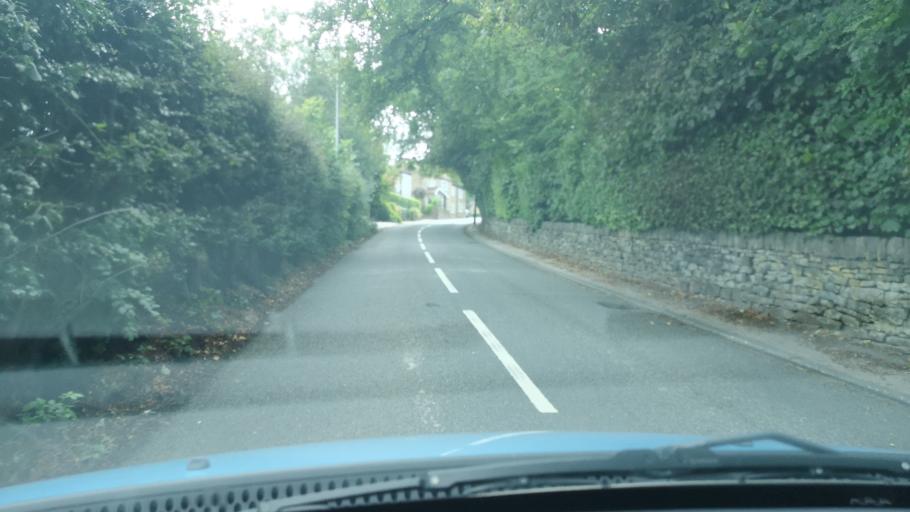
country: GB
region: England
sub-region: Kirklees
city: Mirfield
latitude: 53.6655
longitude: -1.7024
